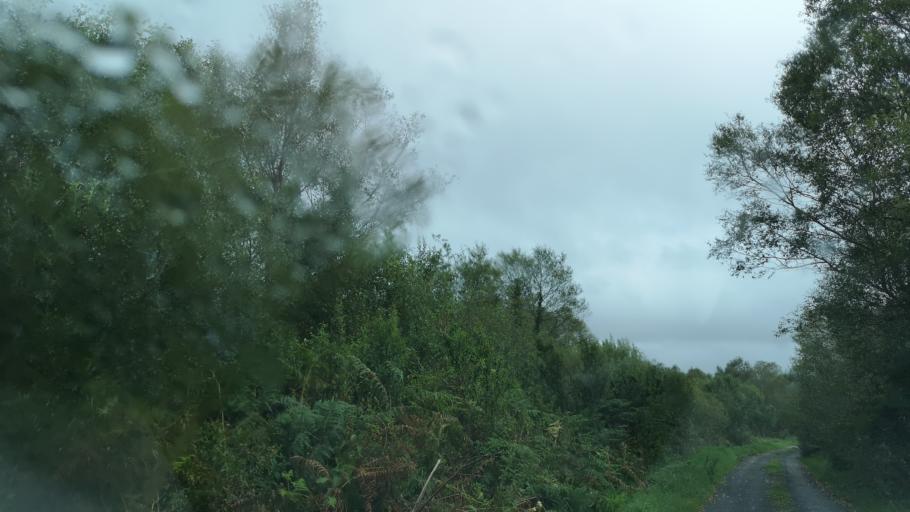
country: IE
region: Connaught
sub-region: County Galway
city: Athenry
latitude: 53.3046
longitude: -8.6340
